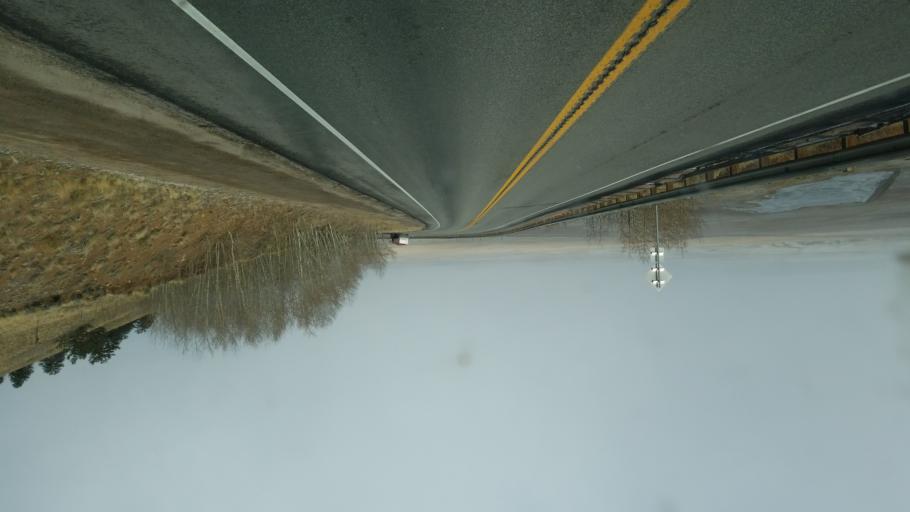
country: US
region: Colorado
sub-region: Summit County
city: Breckenridge
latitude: 39.4019
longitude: -105.7600
